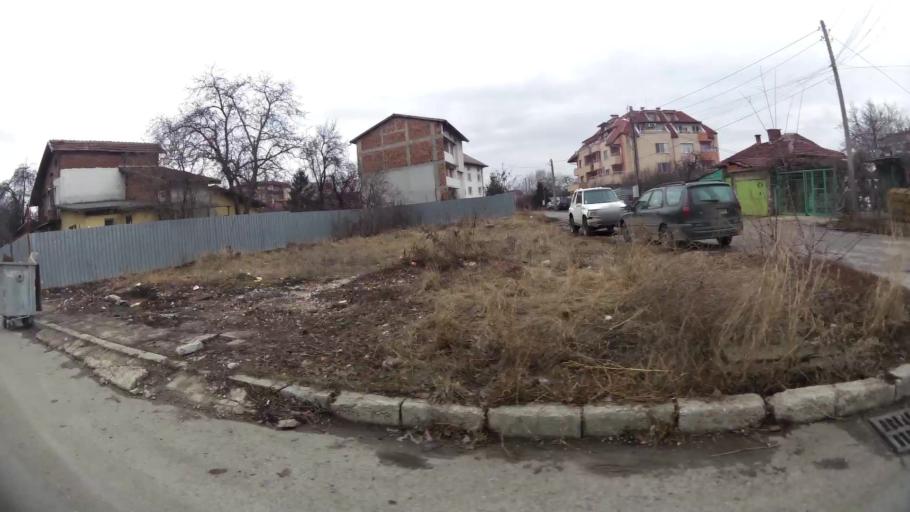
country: BG
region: Sofia-Capital
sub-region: Stolichna Obshtina
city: Sofia
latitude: 42.7271
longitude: 23.2666
